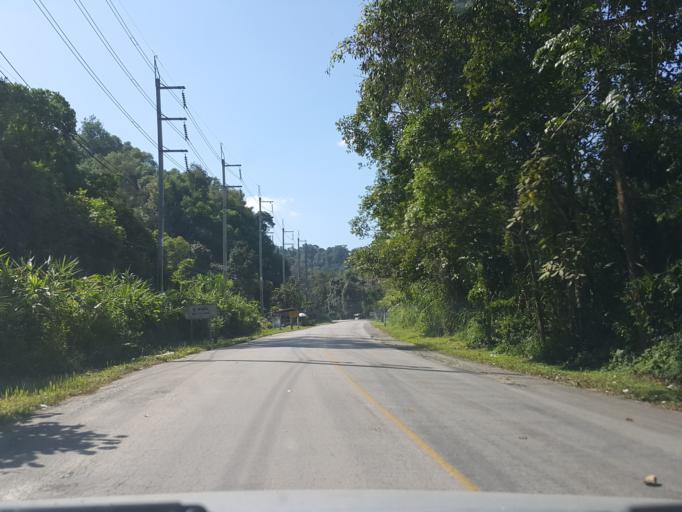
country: TH
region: Chiang Mai
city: Mae Taeng
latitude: 19.1182
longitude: 98.7358
